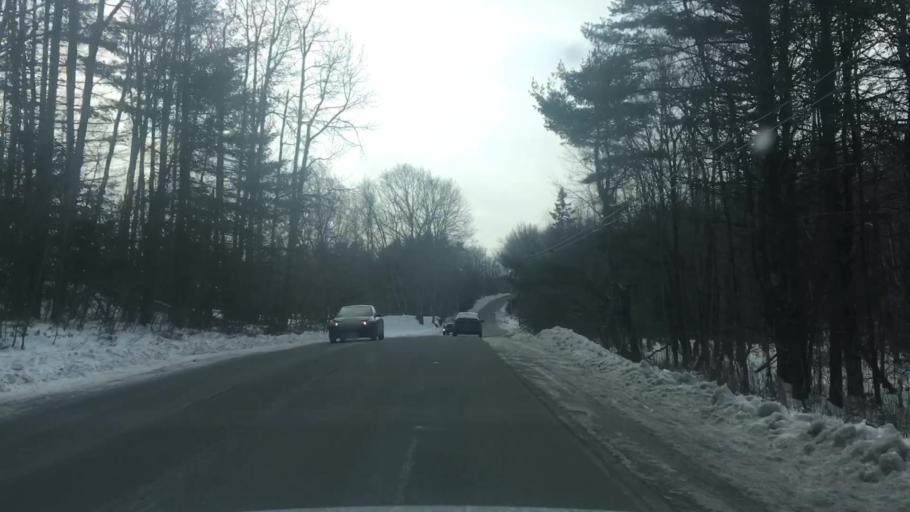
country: US
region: Maine
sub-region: Hancock County
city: Orland
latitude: 44.6145
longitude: -68.7105
